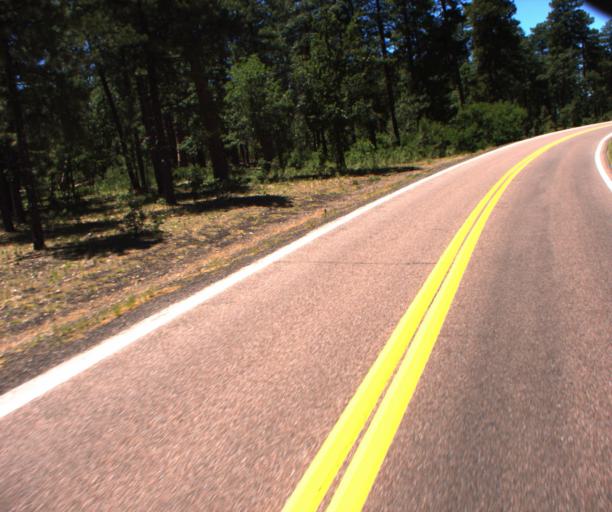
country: US
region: Arizona
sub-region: Gila County
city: Pine
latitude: 34.4414
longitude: -111.4560
